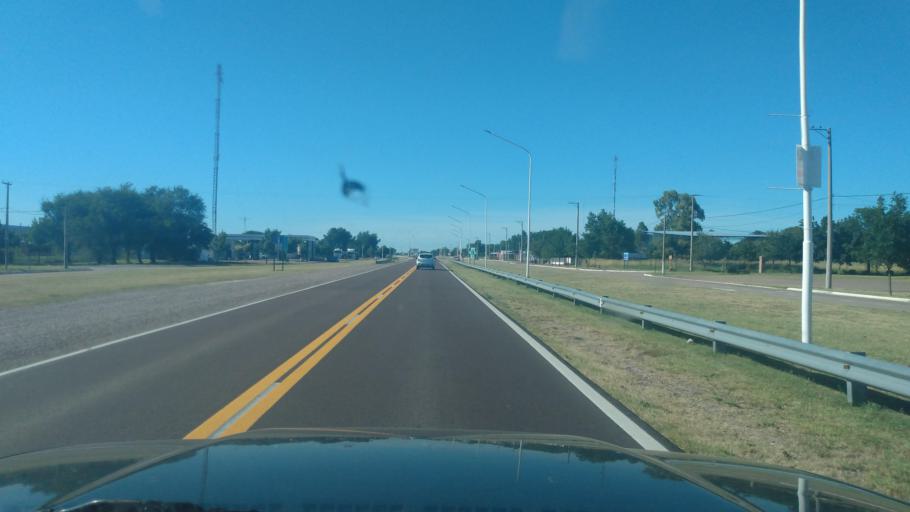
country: AR
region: La Pampa
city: Doblas
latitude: -37.0294
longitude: -64.2889
